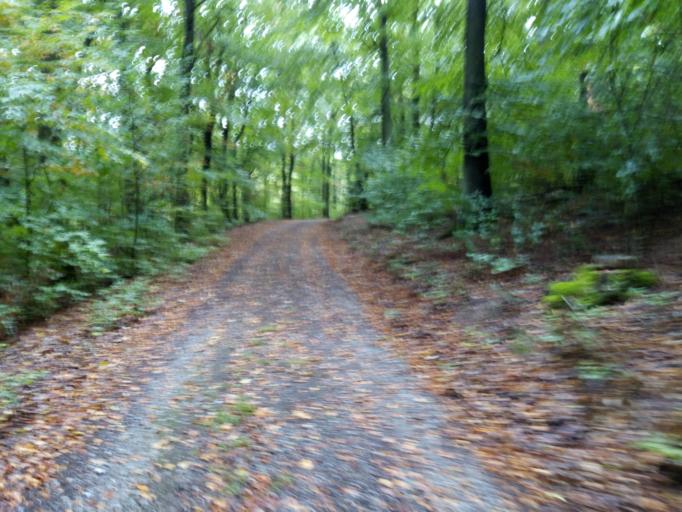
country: DE
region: Rheinland-Pfalz
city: Trechtingshausen
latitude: 49.9875
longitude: 7.8513
